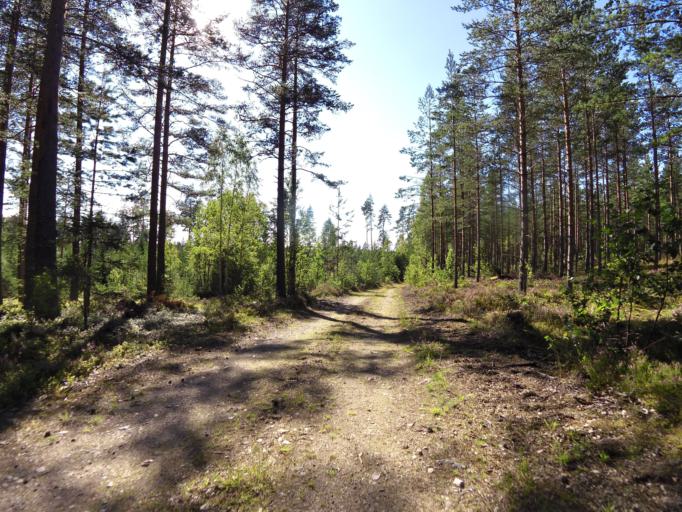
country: SE
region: Gaevleborg
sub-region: Hofors Kommun
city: Hofors
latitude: 60.5726
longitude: 16.4474
